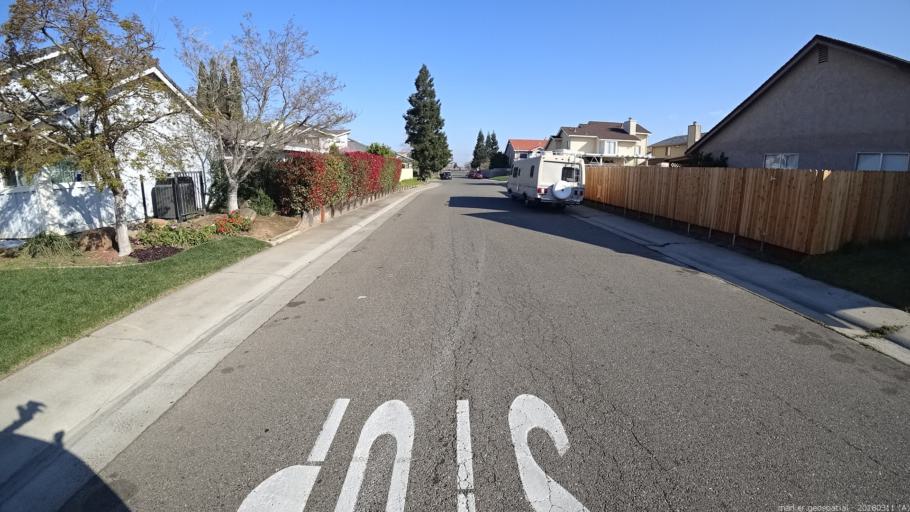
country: US
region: California
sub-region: Sacramento County
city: Florin
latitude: 38.4632
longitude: -121.4046
